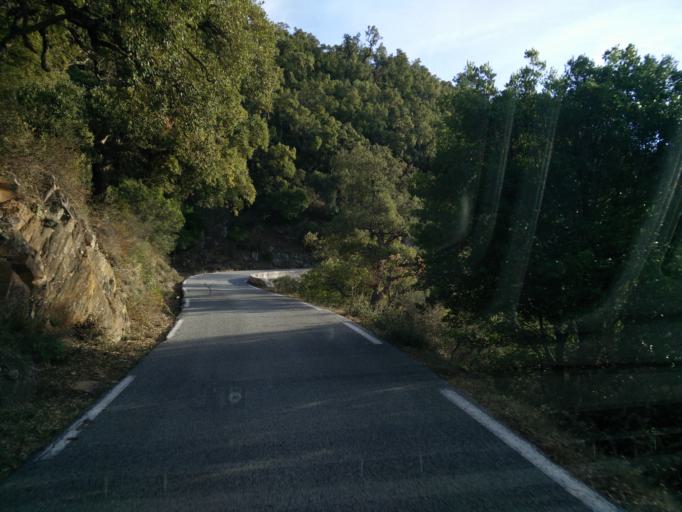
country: FR
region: Provence-Alpes-Cote d'Azur
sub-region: Departement du Var
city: Collobrieres
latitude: 43.1955
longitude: 6.3153
